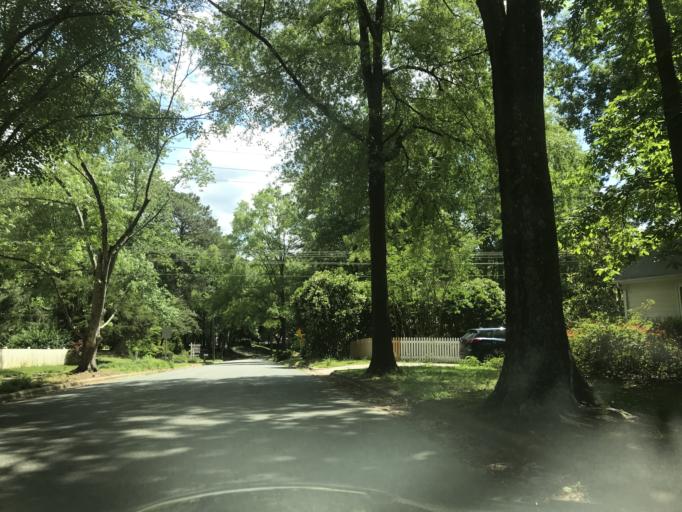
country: US
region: North Carolina
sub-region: Wake County
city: West Raleigh
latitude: 35.8584
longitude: -78.6252
